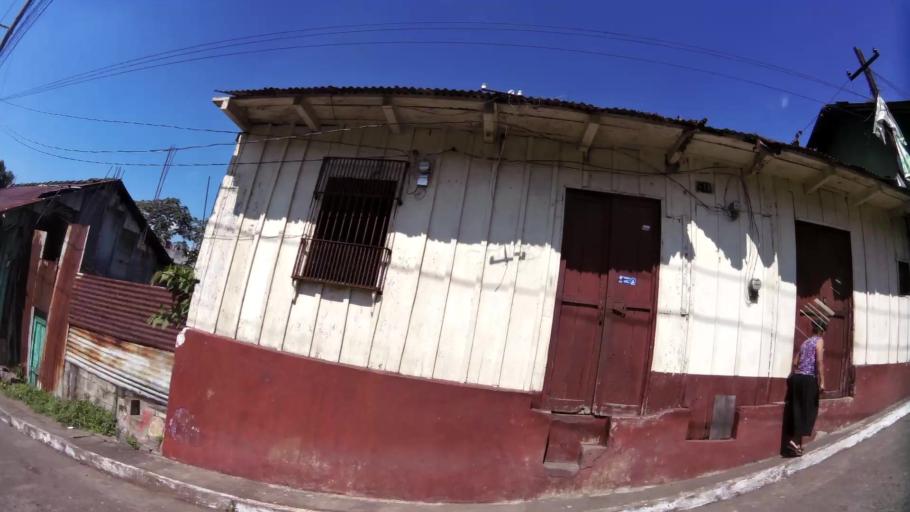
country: GT
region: Suchitepeque
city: Mazatenango
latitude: 14.5339
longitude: -91.5004
